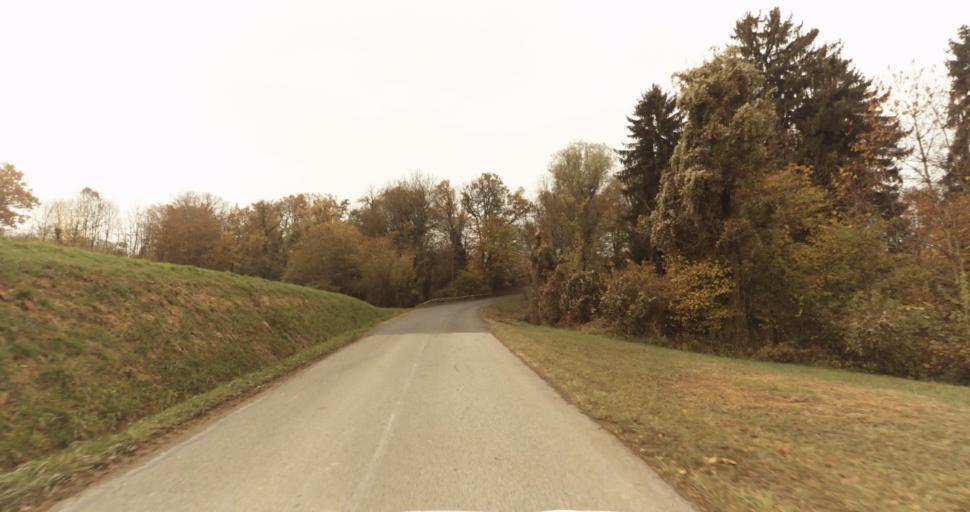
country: FR
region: Rhone-Alpes
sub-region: Departement de la Haute-Savoie
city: Saint-Felix
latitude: 45.7911
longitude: 5.9916
